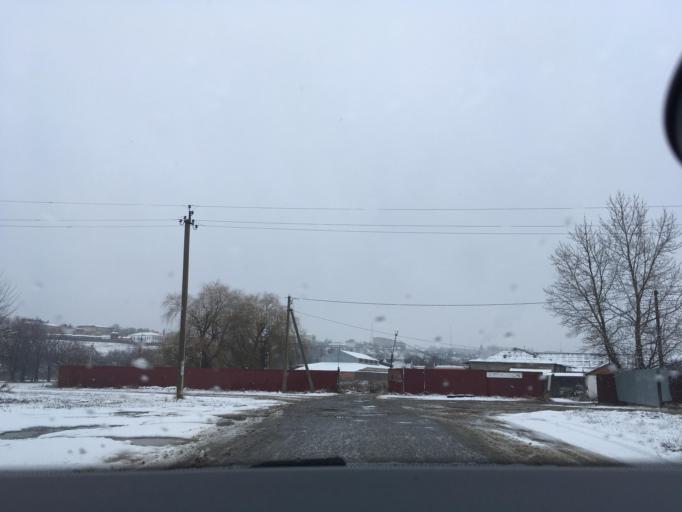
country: RU
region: Belgorod
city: Valuyki
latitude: 50.2053
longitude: 38.1032
